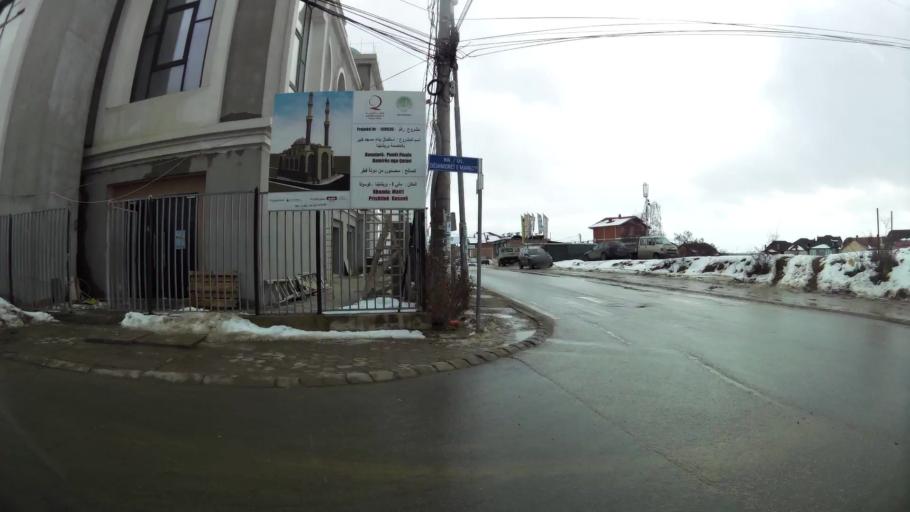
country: XK
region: Pristina
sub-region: Komuna e Prishtines
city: Pristina
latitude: 42.6567
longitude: 21.1874
